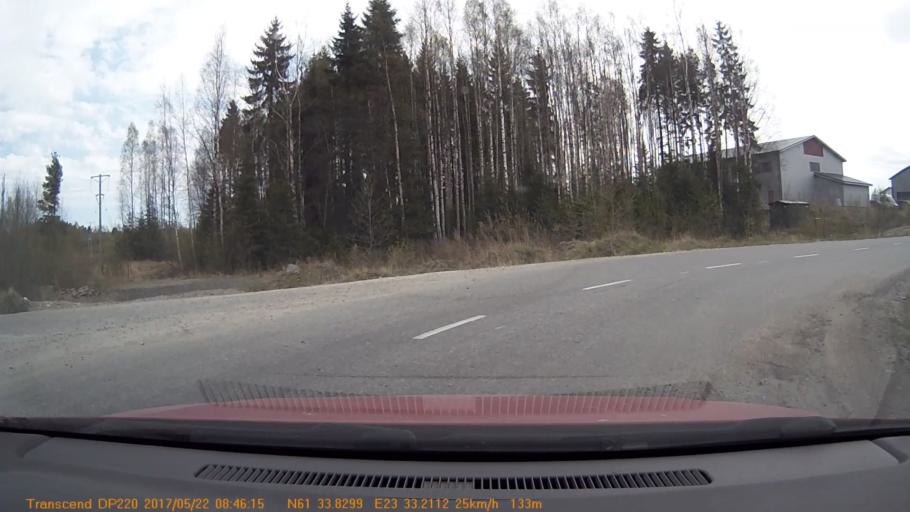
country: FI
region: Pirkanmaa
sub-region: Tampere
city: Yloejaervi
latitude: 61.5638
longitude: 23.5533
